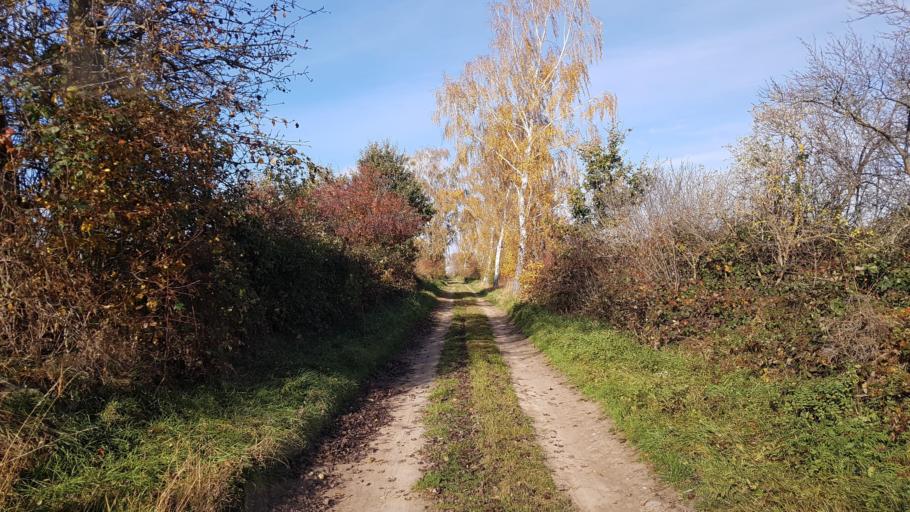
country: DE
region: Saxony-Anhalt
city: Zahna
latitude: 51.9704
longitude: 12.8385
